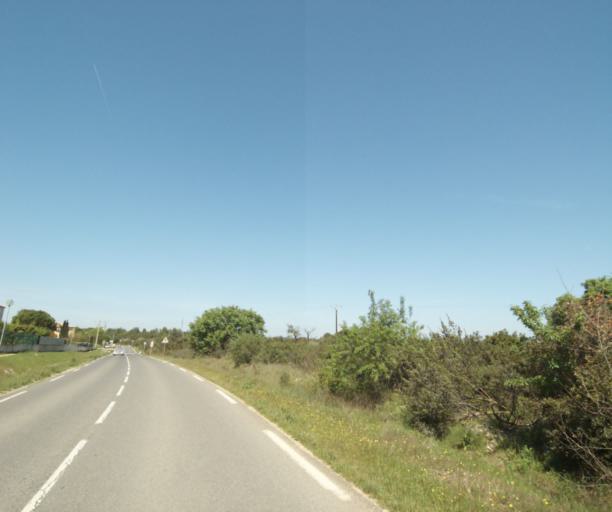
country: FR
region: Languedoc-Roussillon
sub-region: Departement de l'Herault
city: Saint-Bres
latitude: 43.6707
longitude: 4.0353
